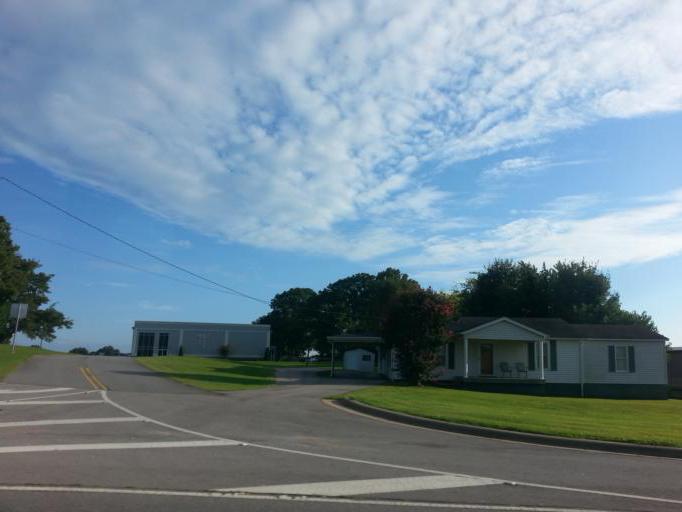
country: US
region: Alabama
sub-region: Lauderdale County
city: Rogersville
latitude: 34.8469
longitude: -87.3839
